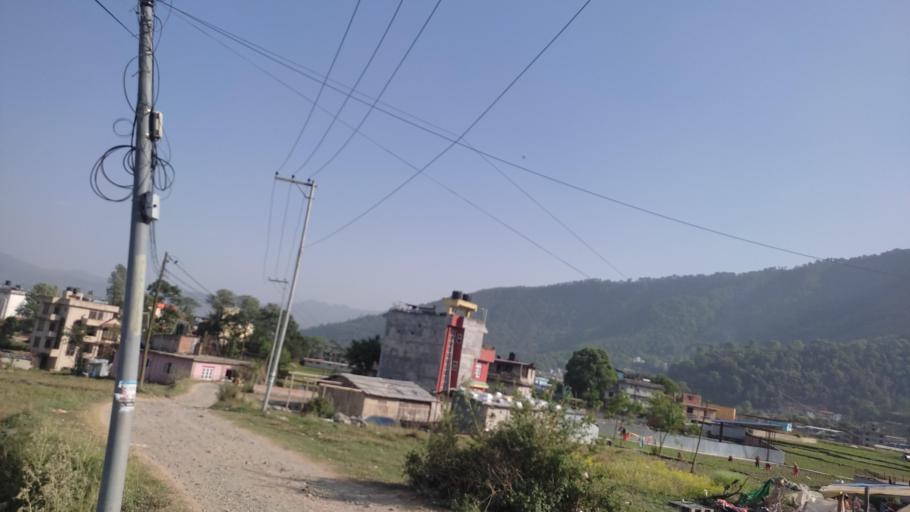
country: NP
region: Central Region
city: Kirtipur
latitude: 27.6544
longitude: 85.2795
